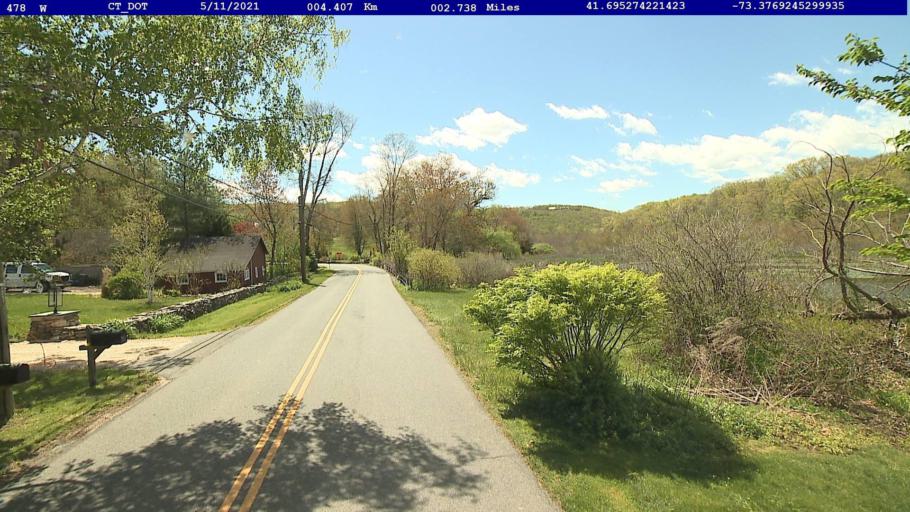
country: US
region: Connecticut
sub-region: Litchfield County
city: New Preston
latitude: 41.6952
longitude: -73.3770
